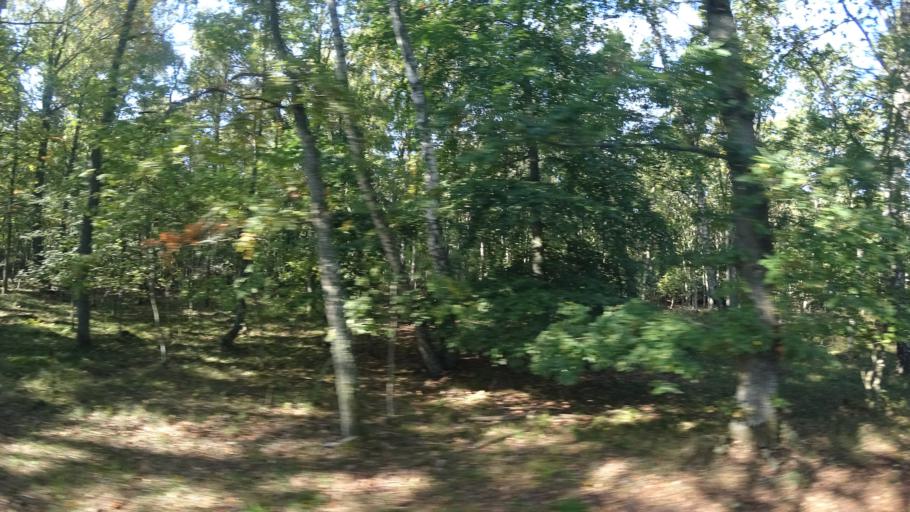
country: SE
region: Skane
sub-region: Kristianstads Kommun
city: Ahus
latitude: 55.9204
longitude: 14.3196
